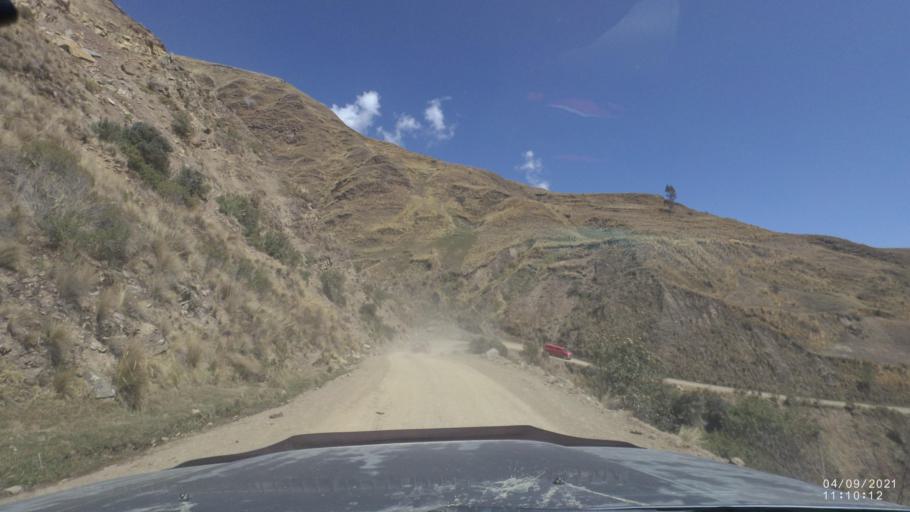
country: BO
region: Cochabamba
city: Sipe Sipe
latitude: -17.2783
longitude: -66.4814
